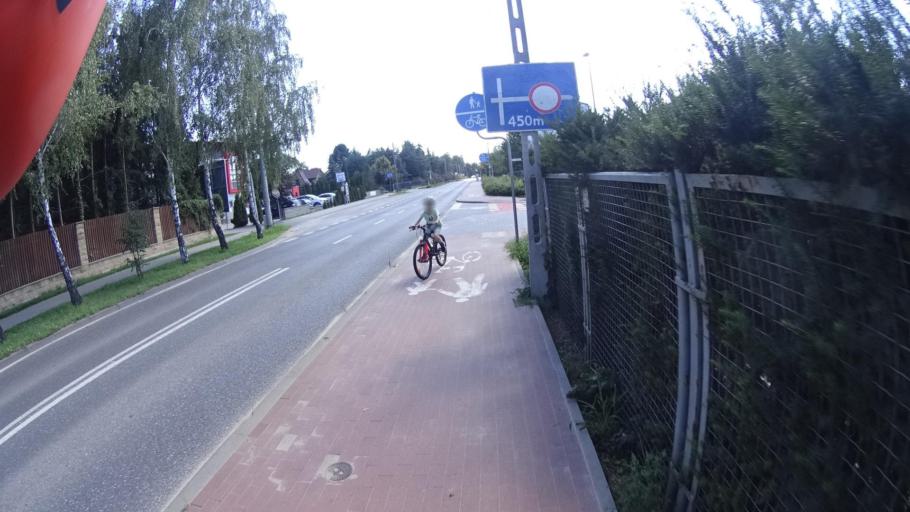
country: PL
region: Masovian Voivodeship
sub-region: Powiat piaseczynski
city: Jozefoslaw
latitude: 52.0935
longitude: 21.0515
